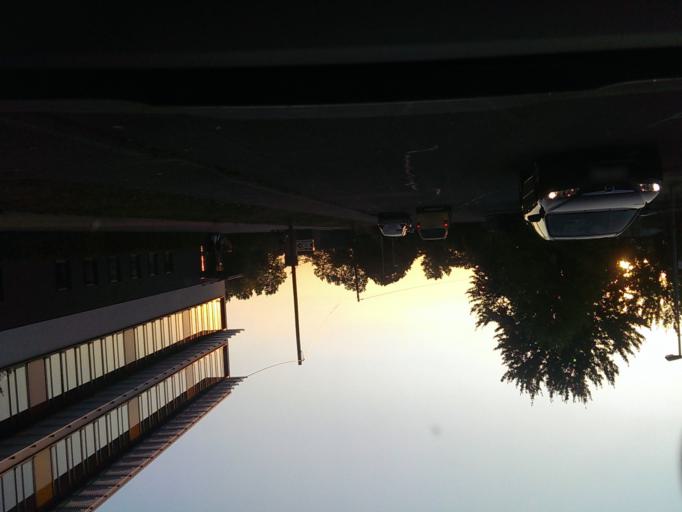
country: DE
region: Baden-Wuerttemberg
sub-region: Karlsruhe Region
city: Karlsruhe
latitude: 49.0310
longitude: 8.3866
